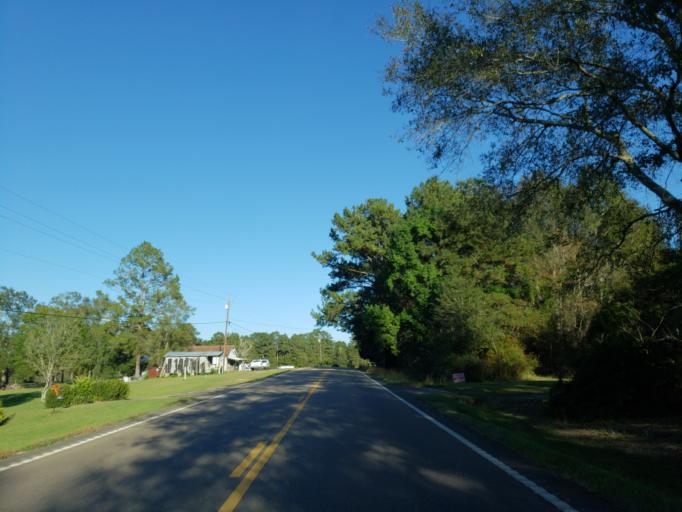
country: US
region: Mississippi
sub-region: Perry County
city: Richton
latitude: 31.3758
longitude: -88.8583
